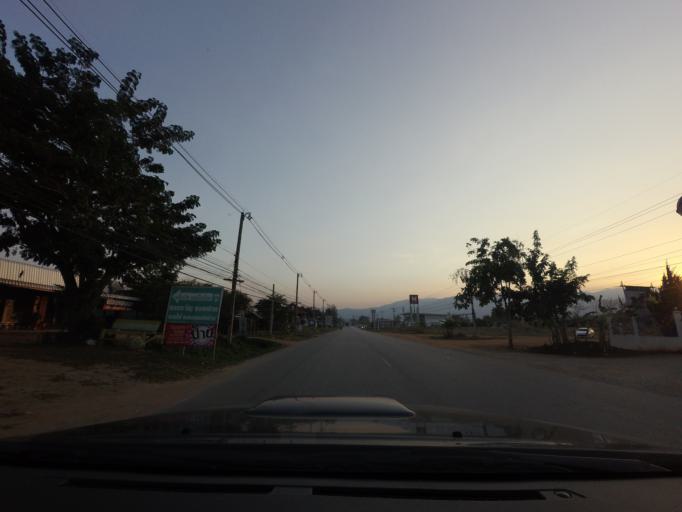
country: TH
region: Chiang Mai
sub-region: Amphoe Chiang Dao
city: Chiang Dao
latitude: 19.3525
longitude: 98.9631
